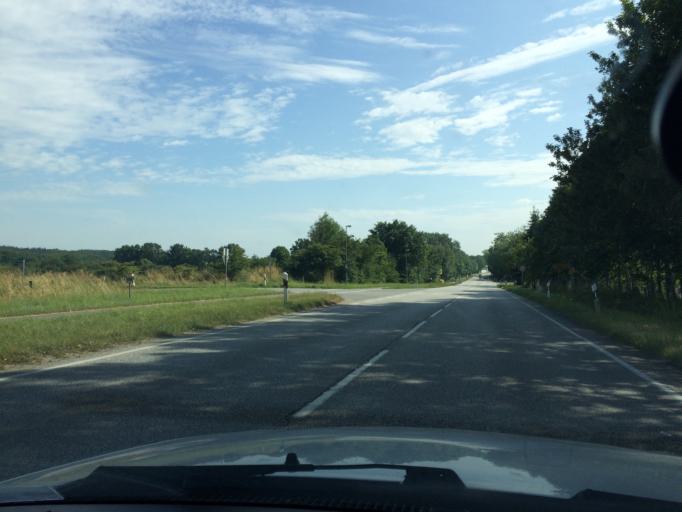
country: DE
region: Schleswig-Holstein
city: Oeversee
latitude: 54.7076
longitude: 9.4385
